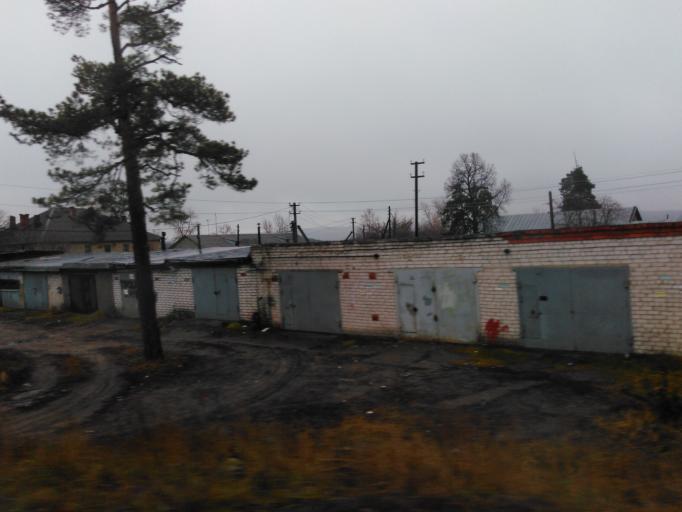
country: RU
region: Tatarstan
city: Osinovo
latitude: 55.8192
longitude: 48.8738
